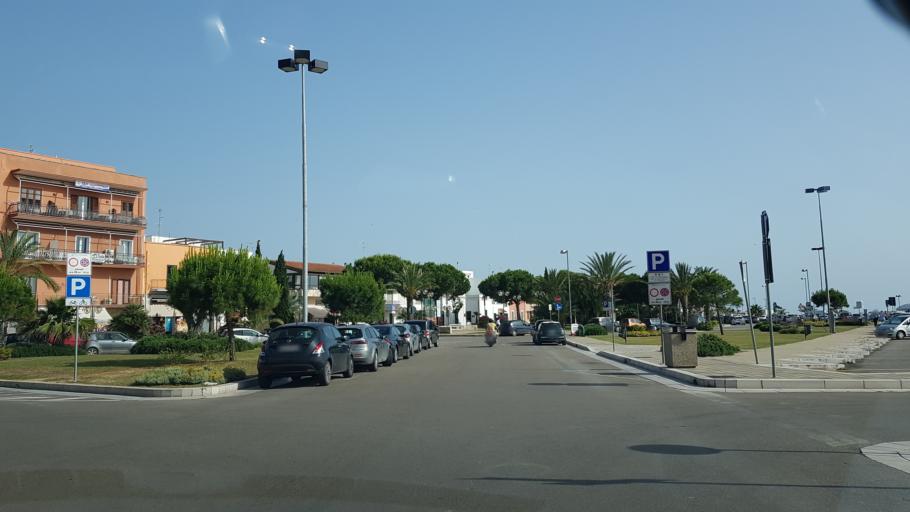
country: IT
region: Apulia
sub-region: Provincia di Lecce
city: Porto Cesareo
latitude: 40.2600
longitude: 17.8914
